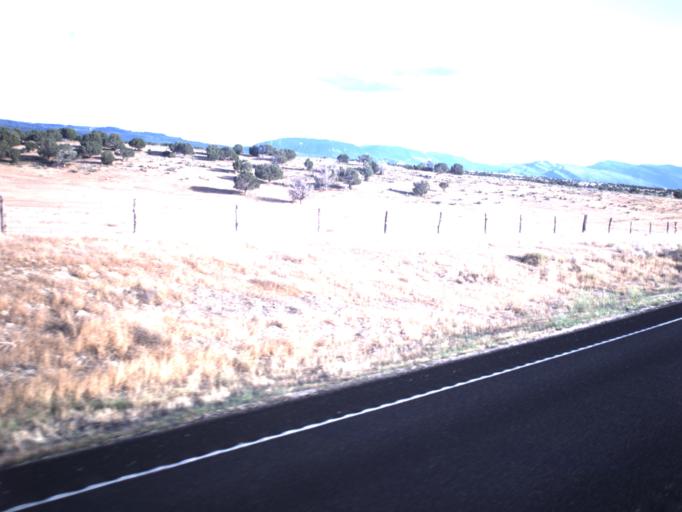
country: US
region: Utah
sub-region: Sanpete County
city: Moroni
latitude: 39.4540
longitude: -111.5421
